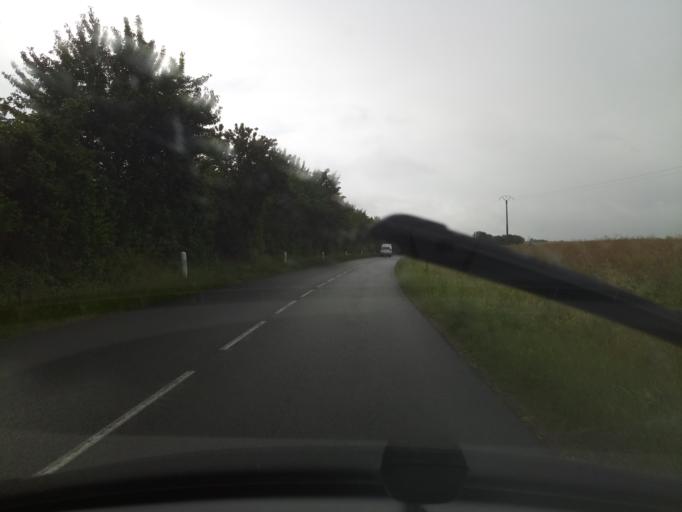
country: FR
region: Poitou-Charentes
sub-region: Departement de la Charente-Maritime
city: Surgeres
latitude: 46.1517
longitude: -0.8119
